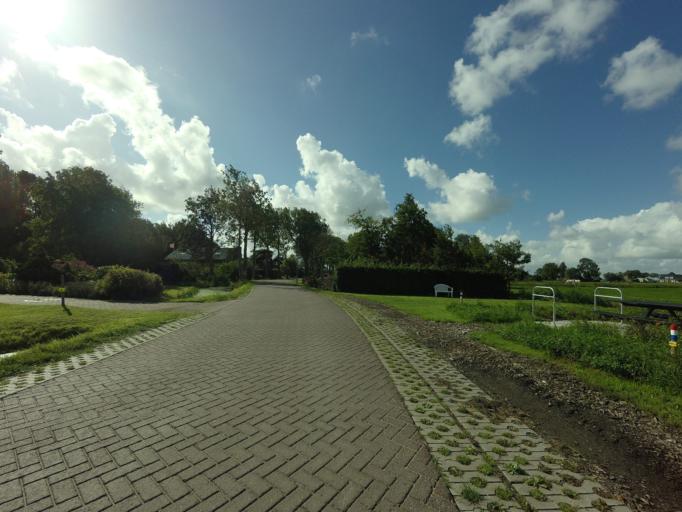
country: NL
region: North Holland
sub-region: Gemeente Hoorn
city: Hoorn
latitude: 52.6548
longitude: 4.9990
